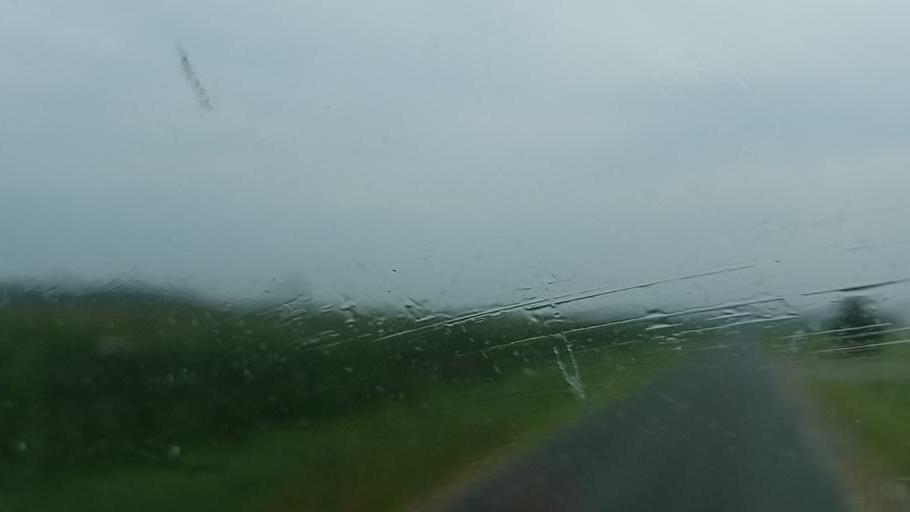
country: US
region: Delaware
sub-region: Sussex County
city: Selbyville
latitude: 38.4426
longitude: -75.2888
